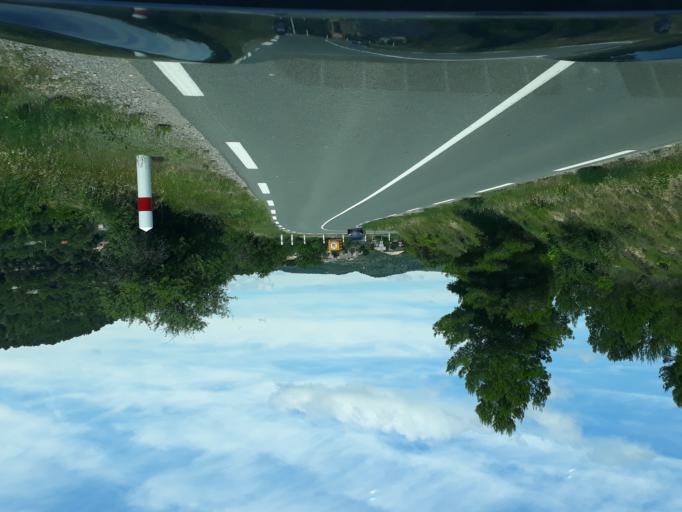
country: FR
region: Languedoc-Roussillon
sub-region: Departement de l'Aude
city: Portel-des-Corbieres
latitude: 43.0462
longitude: 2.9272
